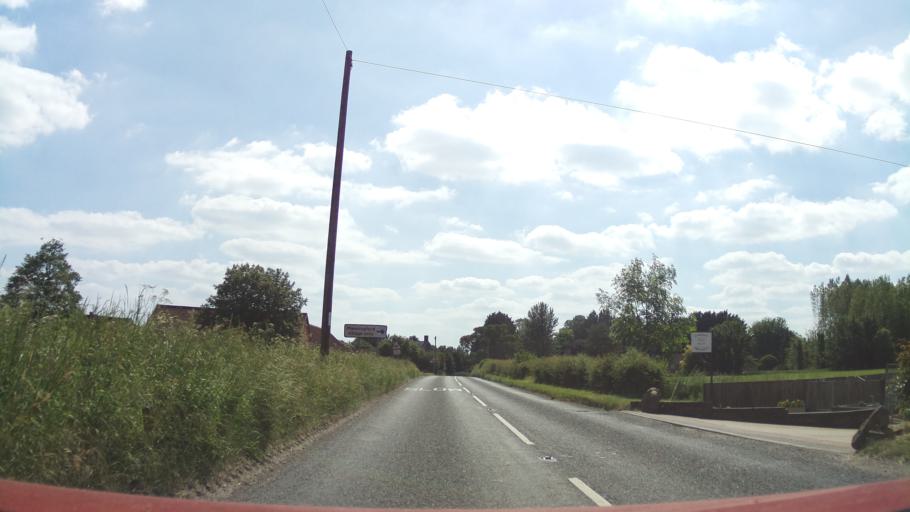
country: GB
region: England
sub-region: Wiltshire
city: Pewsey
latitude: 51.3221
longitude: -1.7957
